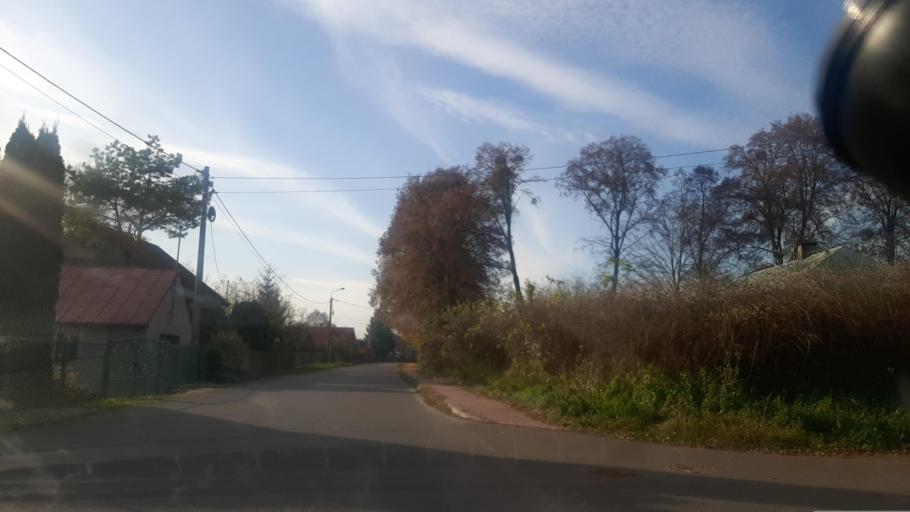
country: PL
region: Lublin Voivodeship
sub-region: Powiat pulawski
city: Markuszow
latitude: 51.3581
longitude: 22.2891
